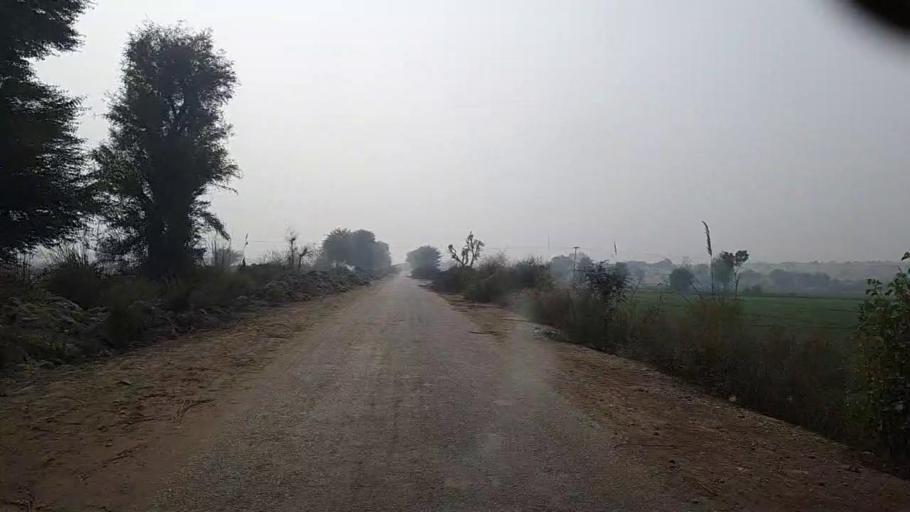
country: PK
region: Sindh
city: Kandiari
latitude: 26.9863
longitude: 68.6034
